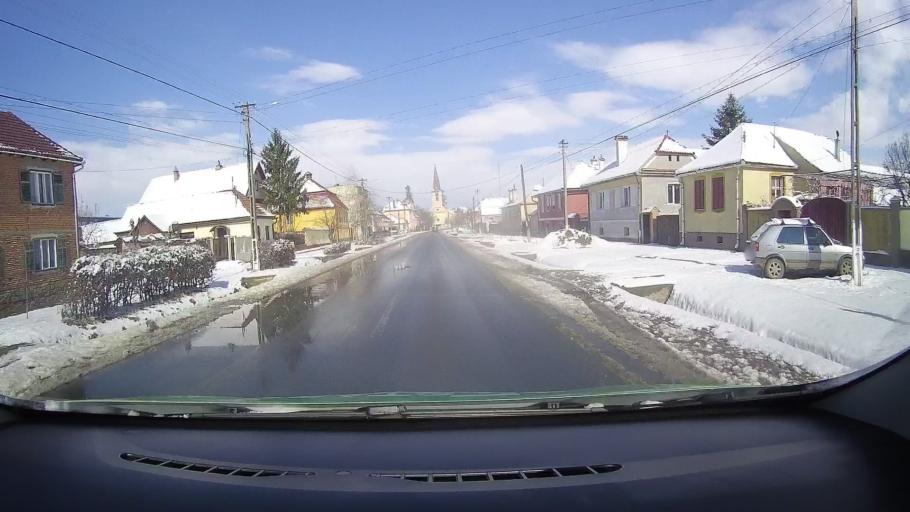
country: RO
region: Sibiu
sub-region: Comuna Nocrich
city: Nocrich
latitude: 45.8928
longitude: 24.4538
